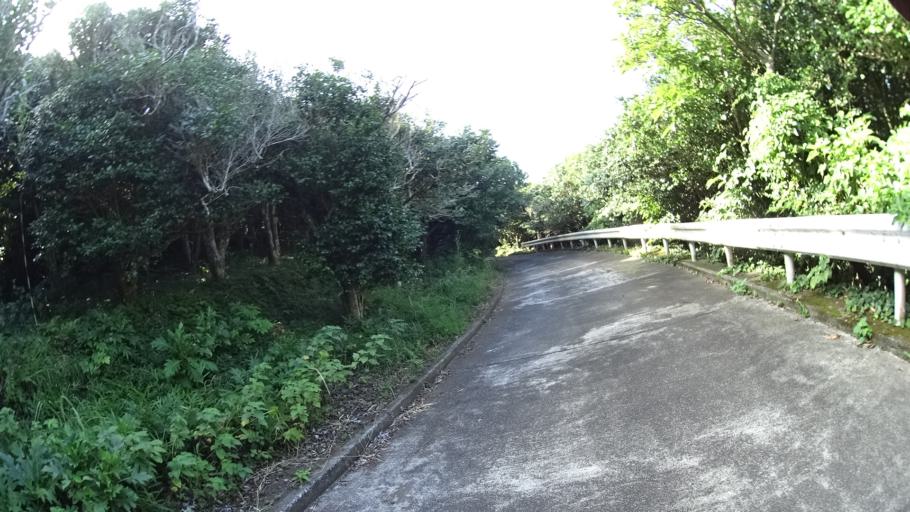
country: JP
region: Shizuoka
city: Shimoda
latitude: 34.5179
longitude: 139.2714
